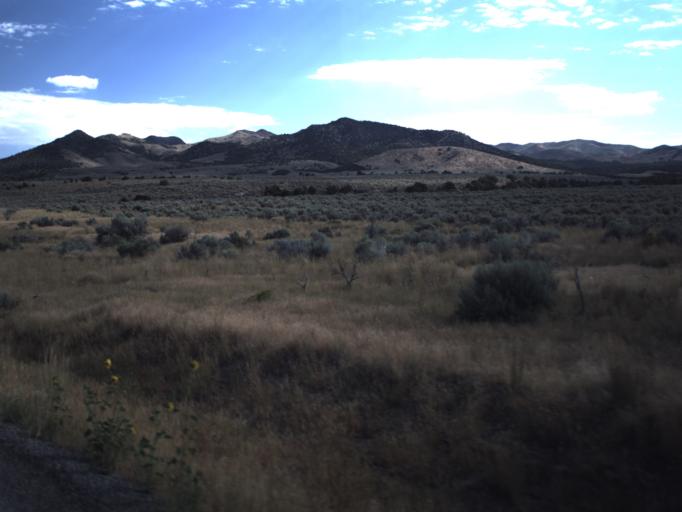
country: US
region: Utah
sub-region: Juab County
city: Mona
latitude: 39.8096
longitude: -112.1434
